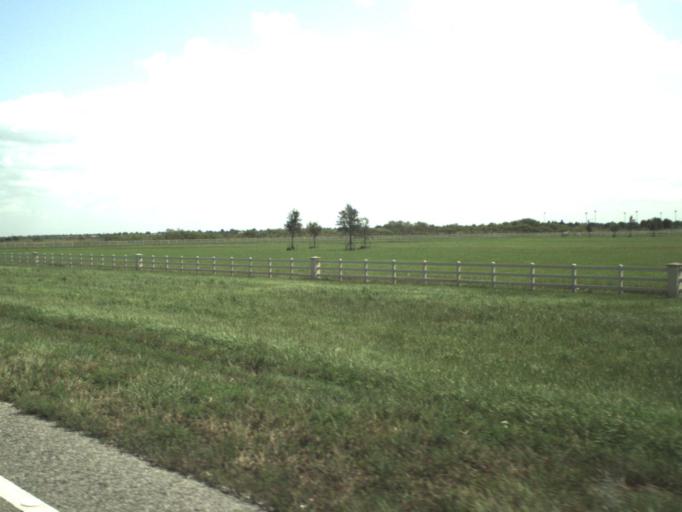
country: US
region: Florida
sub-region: Broward County
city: Weston
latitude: 26.1001
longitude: -80.4341
